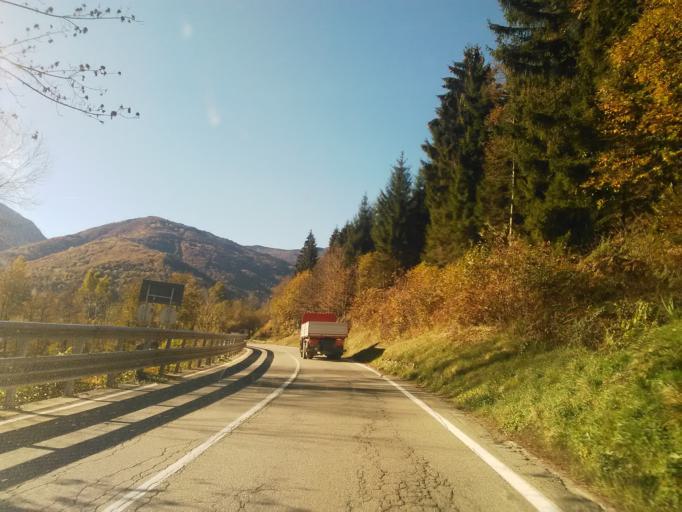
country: IT
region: Piedmont
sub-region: Provincia di Vercelli
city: Scopa
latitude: 45.7829
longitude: 8.1060
